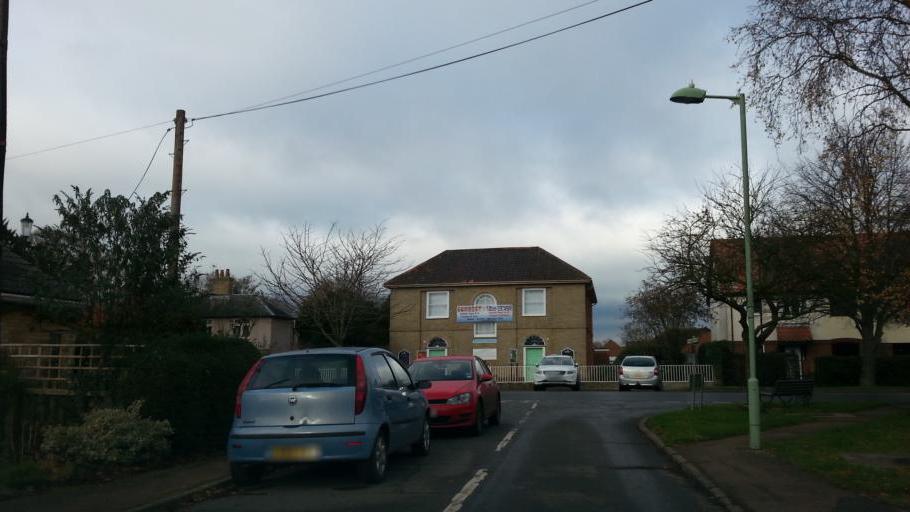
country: GB
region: England
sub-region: Suffolk
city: Framlingham
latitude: 52.3010
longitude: 1.3630
